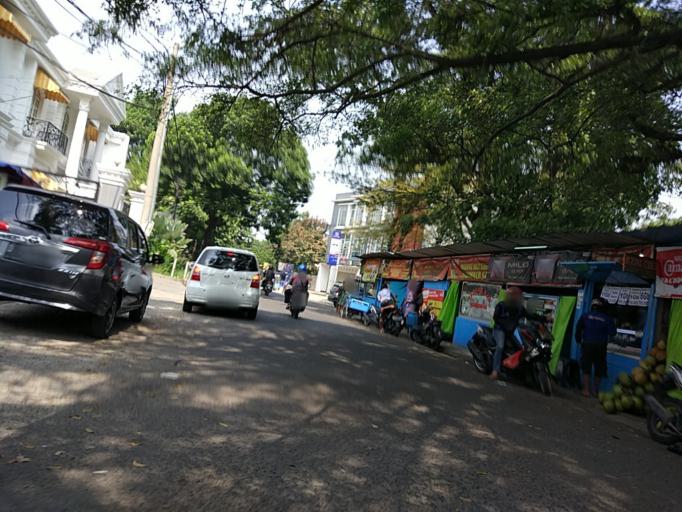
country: ID
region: West Java
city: Margahayukencana
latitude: -6.9327
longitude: 107.5755
